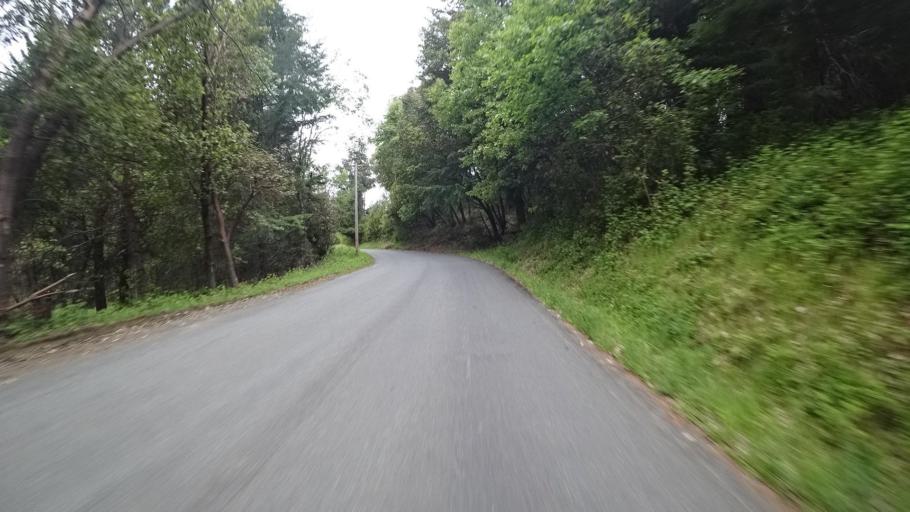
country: US
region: California
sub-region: Humboldt County
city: Willow Creek
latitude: 41.1121
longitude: -123.7153
